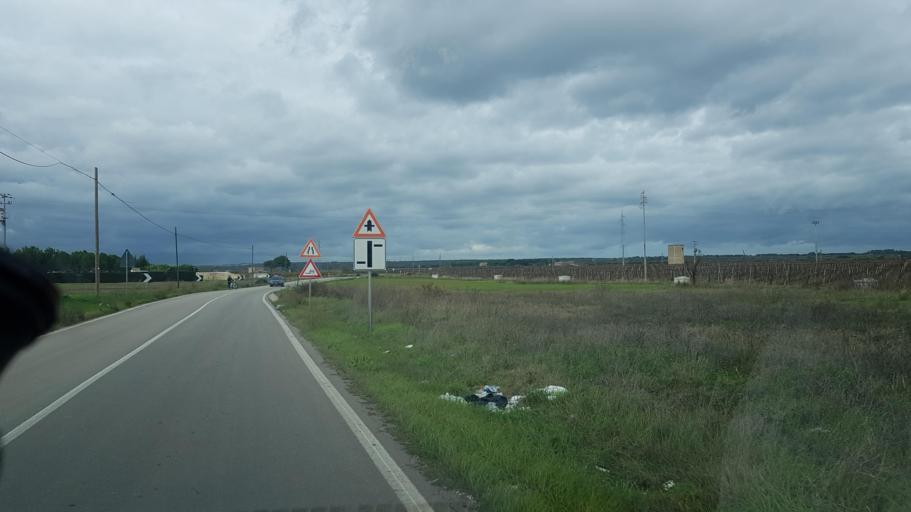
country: IT
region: Apulia
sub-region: Provincia di Brindisi
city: Francavilla Fontana
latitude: 40.5394
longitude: 17.5679
